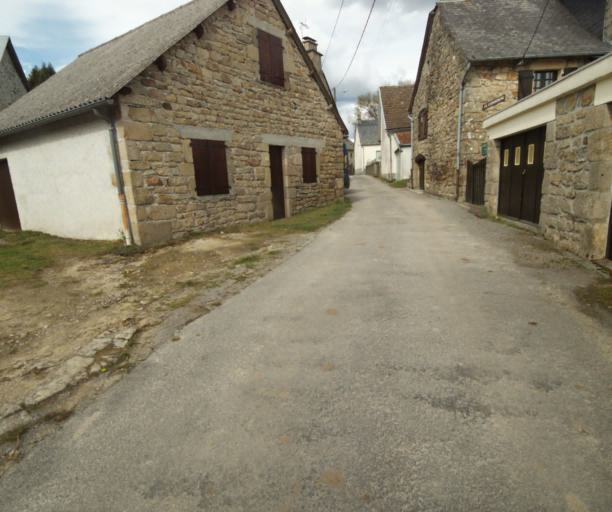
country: FR
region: Limousin
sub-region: Departement de la Correze
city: Argentat
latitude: 45.1790
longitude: 1.9420
